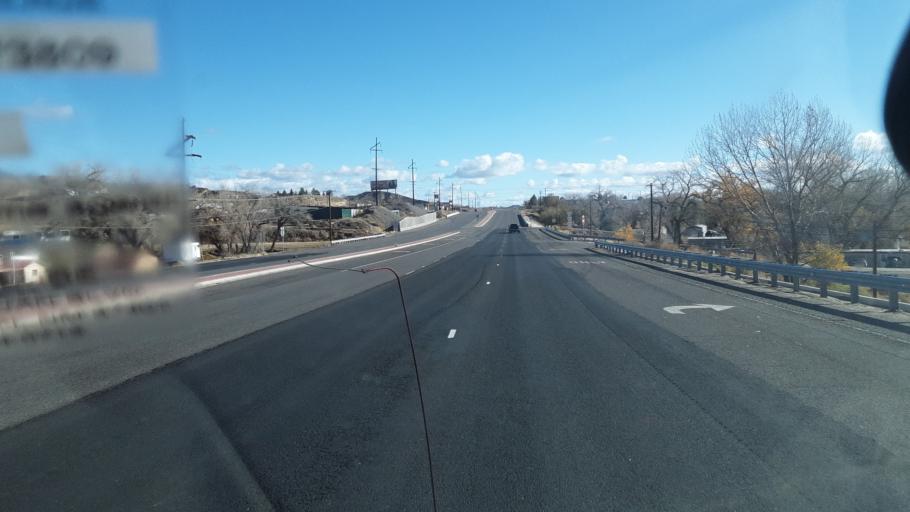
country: US
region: New Mexico
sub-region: San Juan County
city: Lee Acres
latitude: 36.7042
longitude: -108.0272
